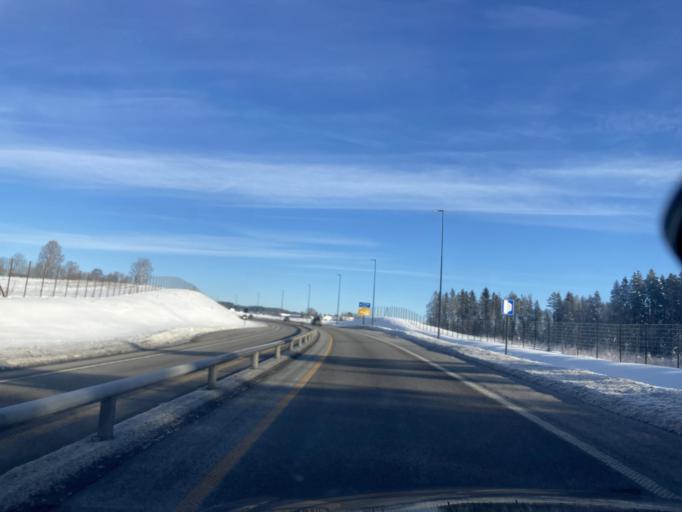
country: NO
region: Hedmark
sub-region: Loten
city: Loten
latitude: 60.8209
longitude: 11.2900
